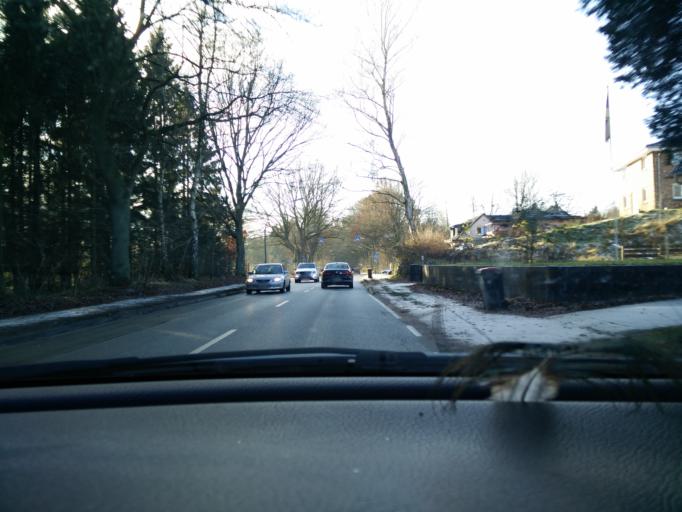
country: DE
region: Hamburg
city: Lemsahl-Mellingstedt
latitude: 53.6908
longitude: 10.0973
